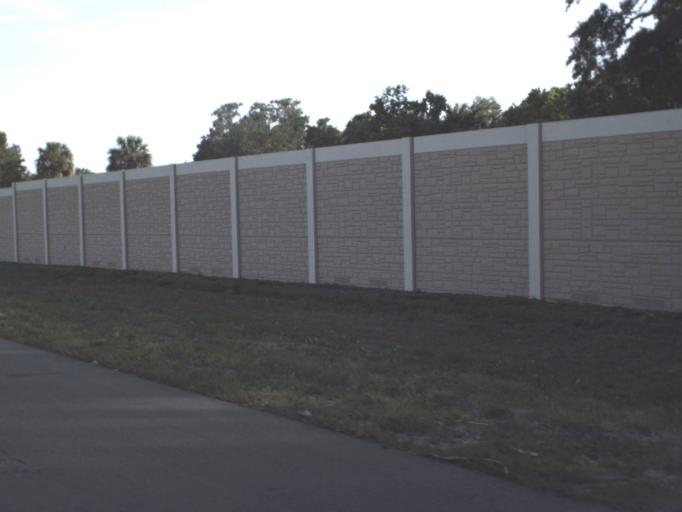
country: US
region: Florida
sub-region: Brevard County
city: Mims
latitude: 28.6497
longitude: -80.8631
